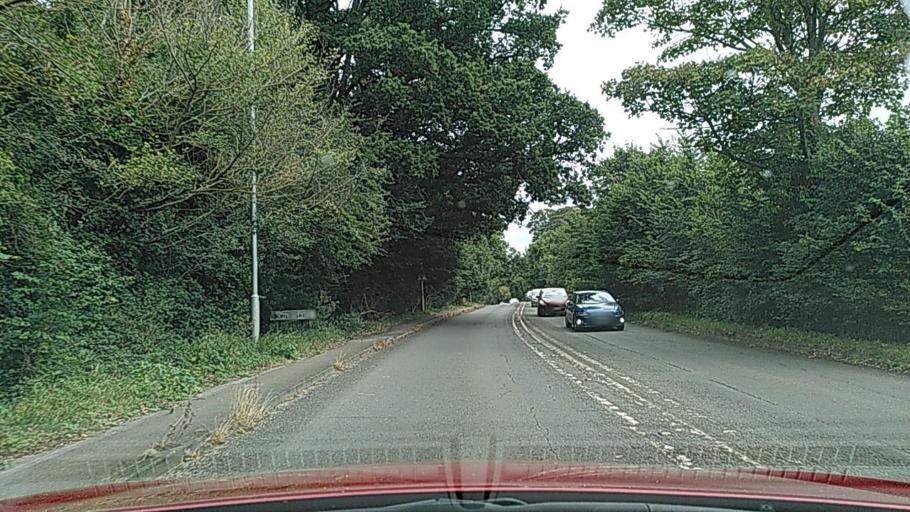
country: GB
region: England
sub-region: Wokingham
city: Wargrave
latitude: 51.4984
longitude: -0.8332
